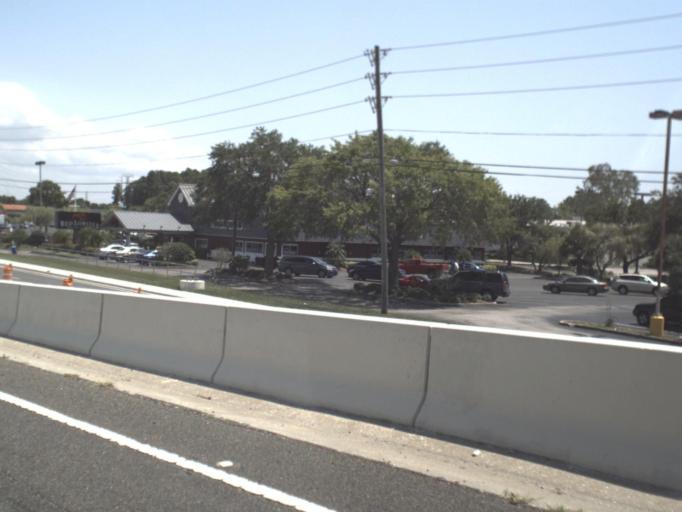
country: US
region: Florida
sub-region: Pinellas County
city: Dunedin
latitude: 28.0128
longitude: -82.7351
